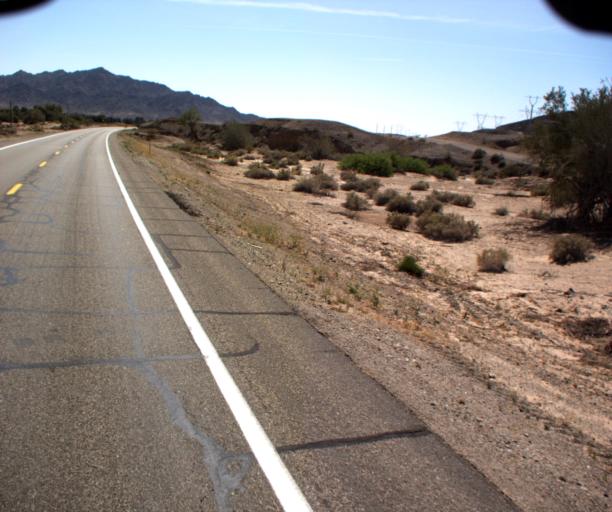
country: US
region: Arizona
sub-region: Yuma County
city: Fortuna Foothills
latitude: 32.7860
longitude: -114.3814
